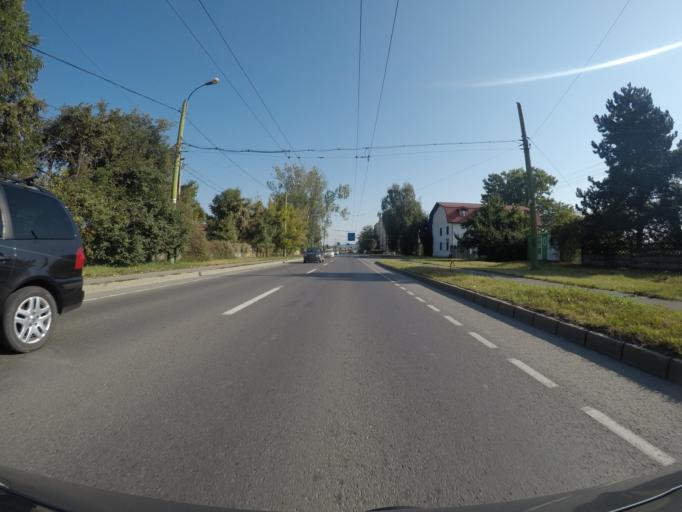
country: RO
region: Brasov
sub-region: Comuna Sanpetru
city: Sanpetru
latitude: 45.6850
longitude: 25.6172
